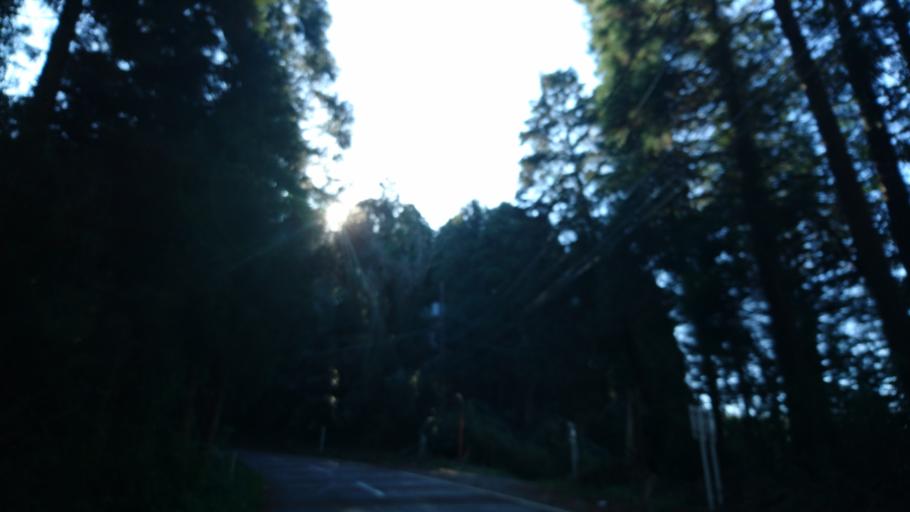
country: JP
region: Chiba
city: Yachimata
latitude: 35.6151
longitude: 140.3366
